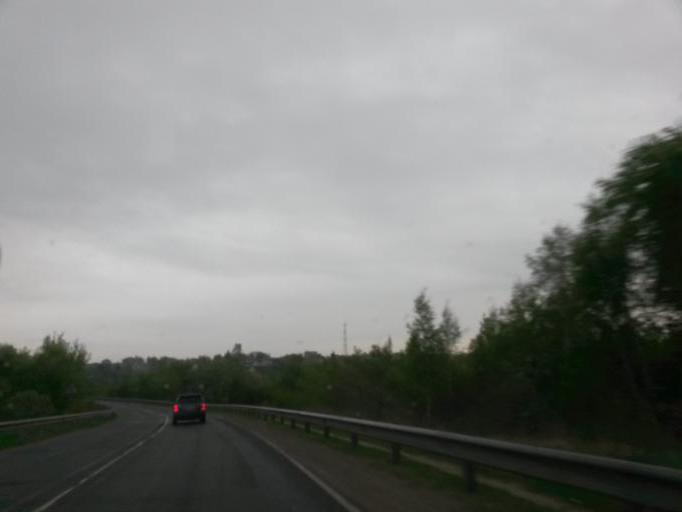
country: RU
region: Moskovskaya
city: Gorki-Leninskiye
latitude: 55.4845
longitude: 37.7793
